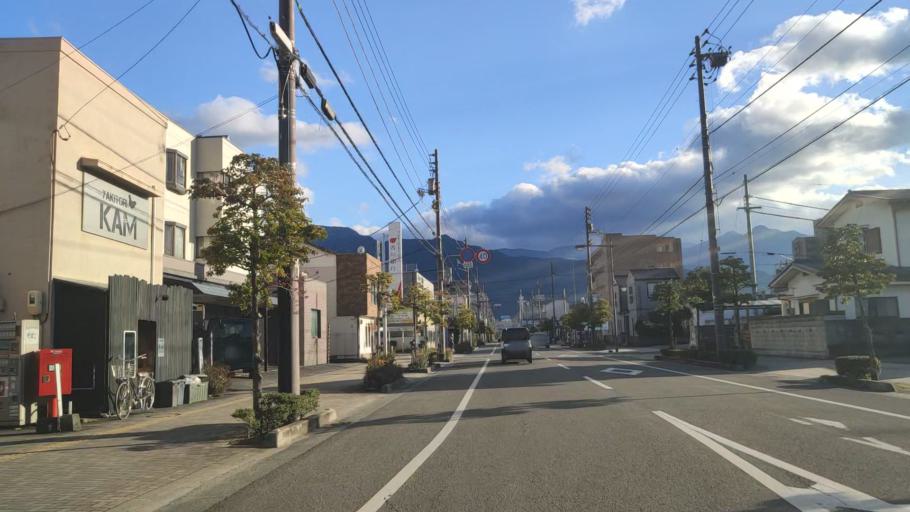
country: JP
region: Ehime
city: Saijo
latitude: 33.9174
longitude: 133.1859
